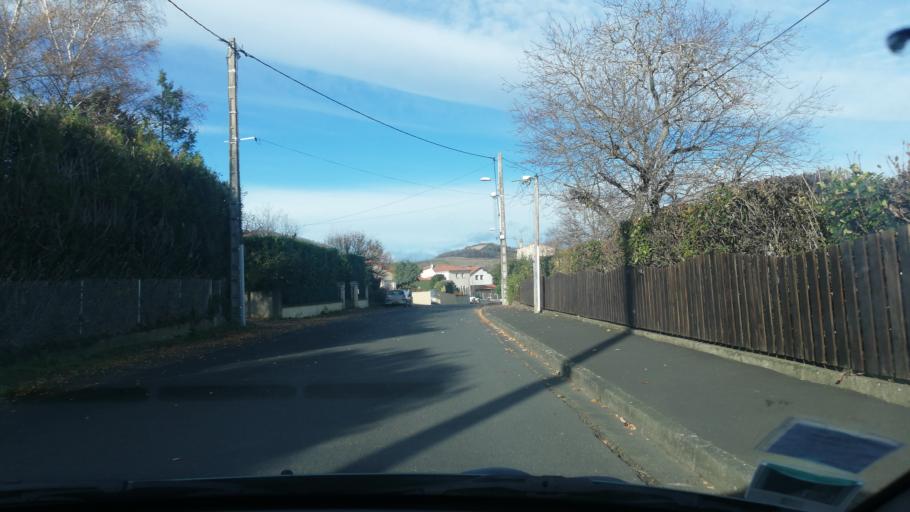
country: FR
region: Auvergne
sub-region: Departement du Puy-de-Dome
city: Billom
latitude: 45.7175
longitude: 3.3421
